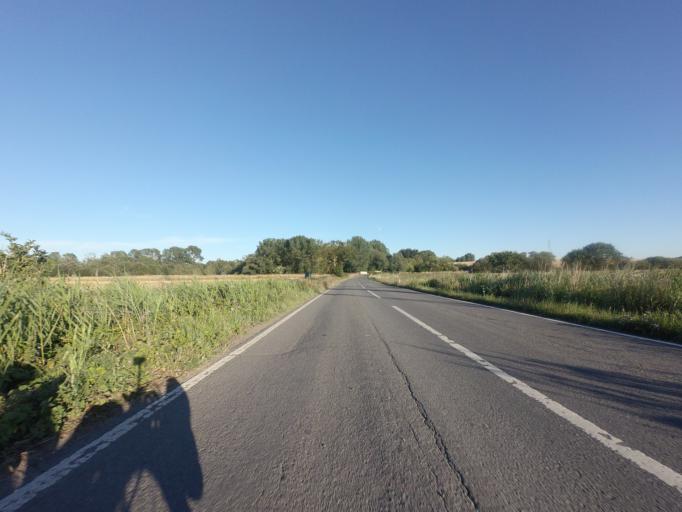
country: GB
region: England
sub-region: Kent
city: Sturry
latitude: 51.3293
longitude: 1.1912
